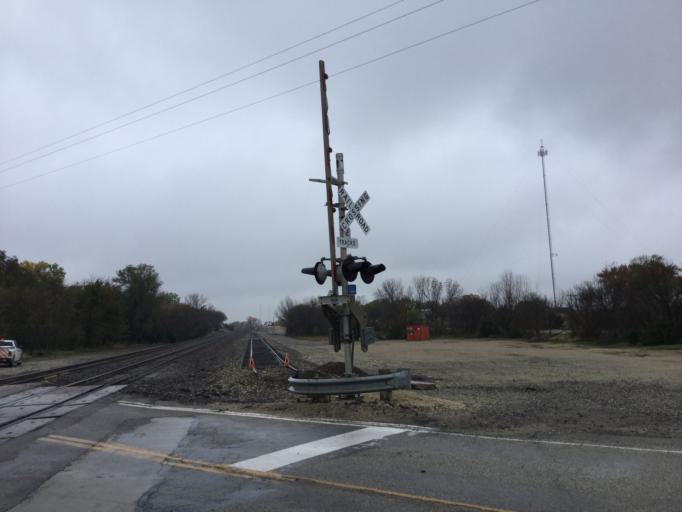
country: US
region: Kansas
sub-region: Butler County
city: El Dorado
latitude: 38.0370
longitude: -96.6393
